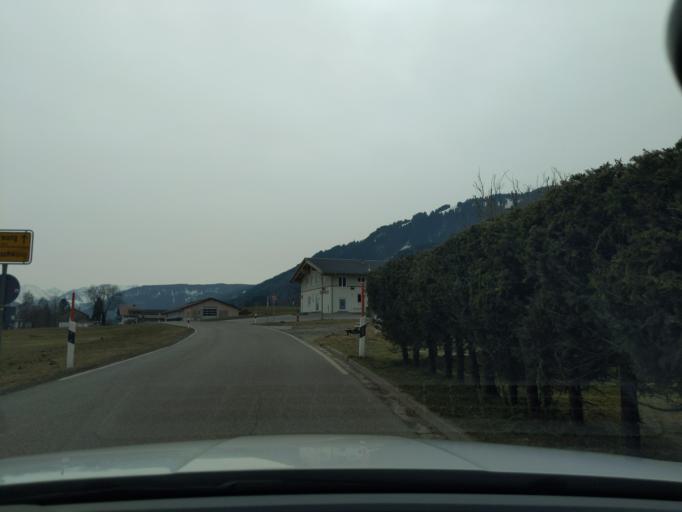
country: DE
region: Bavaria
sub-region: Swabia
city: Ofterschwang
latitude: 47.4917
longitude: 10.2344
